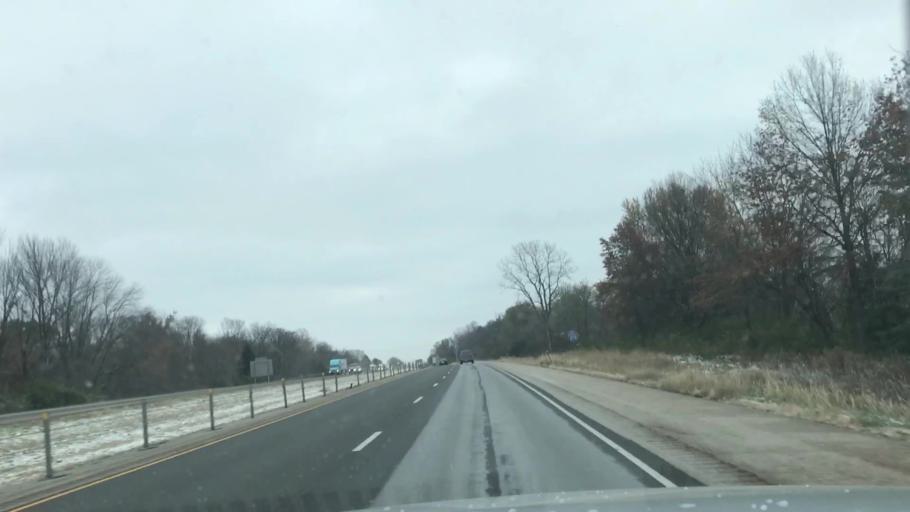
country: US
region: Illinois
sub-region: Madison County
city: Maryville
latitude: 38.7536
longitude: -89.9472
